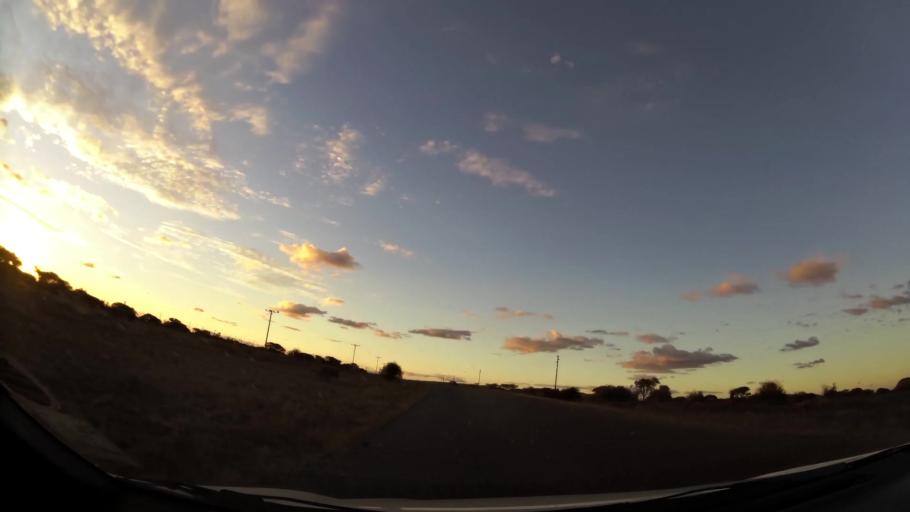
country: ZA
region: Limpopo
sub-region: Capricorn District Municipality
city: Polokwane
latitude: -23.7645
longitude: 29.4747
